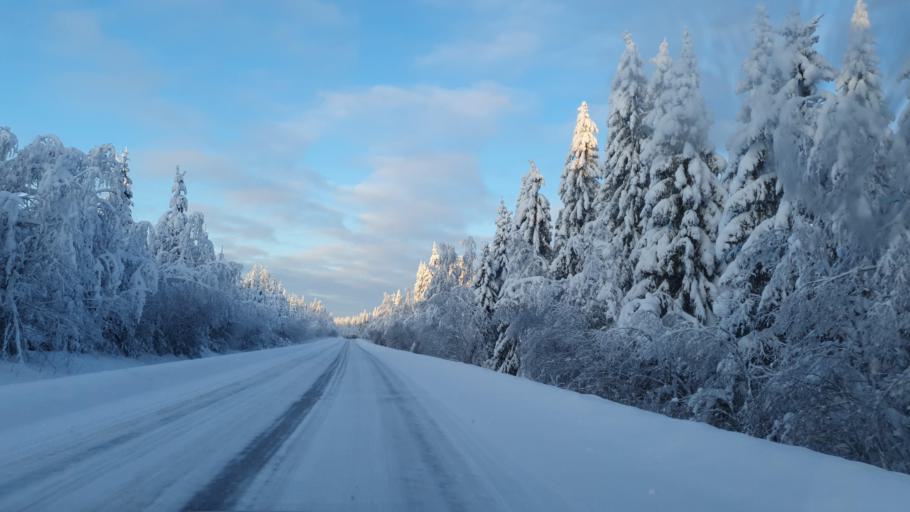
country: FI
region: Kainuu
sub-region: Kajaani
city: Vuokatti
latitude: 64.2216
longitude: 28.2501
